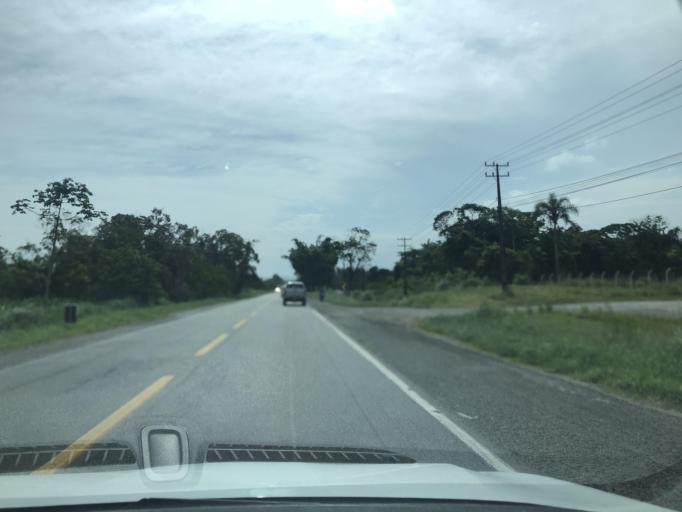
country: BR
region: Santa Catarina
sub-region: Sao Francisco Do Sul
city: Sao Francisco do Sul
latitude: -26.3707
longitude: -48.6968
